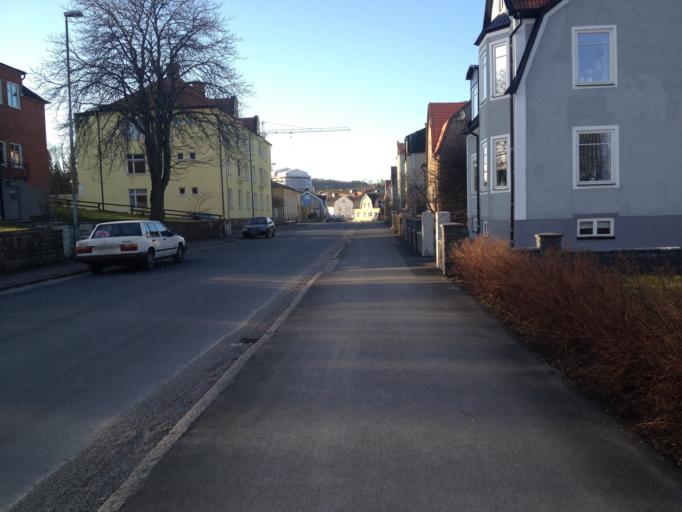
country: SE
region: Vaestra Goetaland
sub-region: Falkopings Kommun
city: Falkoeping
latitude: 58.1712
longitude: 13.5545
